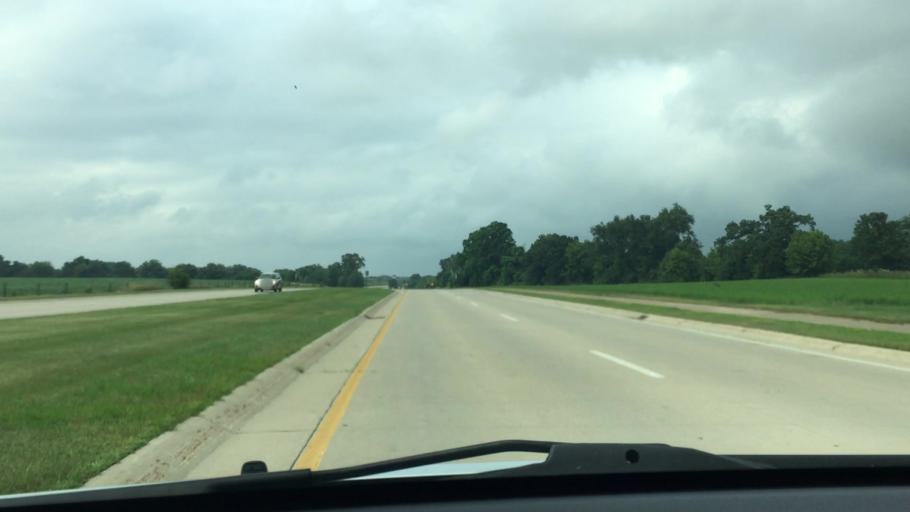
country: US
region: Wisconsin
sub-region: Walworth County
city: Lake Geneva
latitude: 42.5718
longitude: -88.4124
